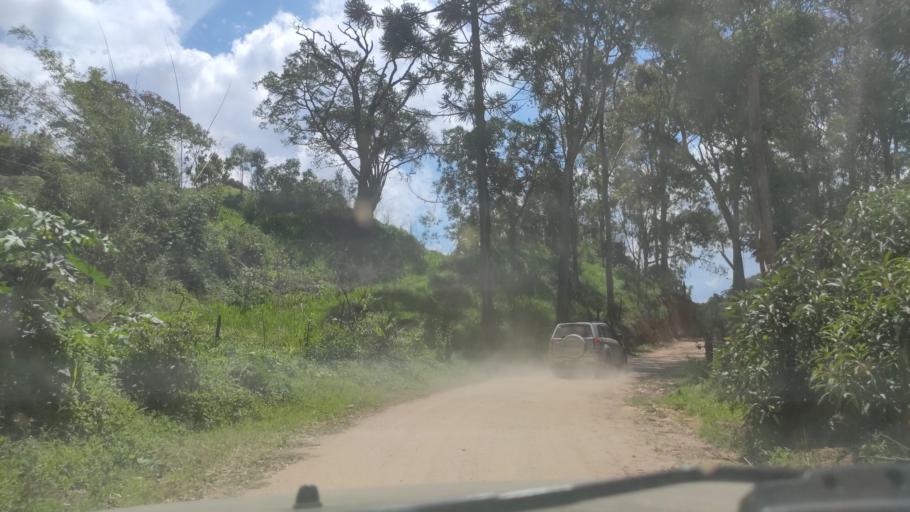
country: BR
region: Minas Gerais
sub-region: Cambui
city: Cambui
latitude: -22.6992
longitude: -45.9972
